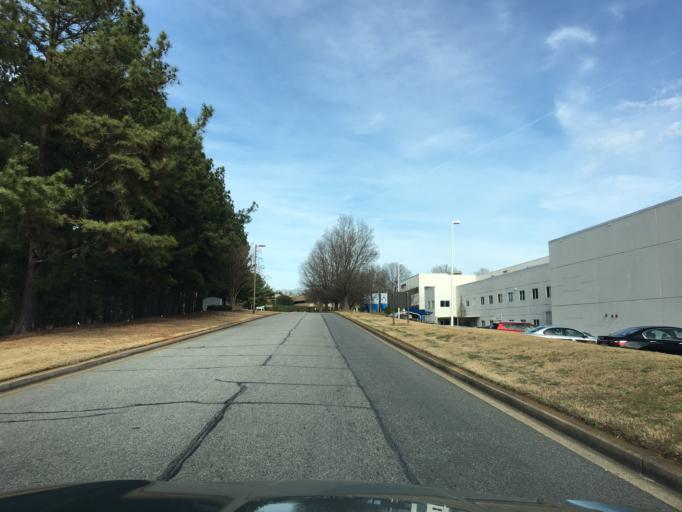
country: US
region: South Carolina
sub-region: Spartanburg County
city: Wellford
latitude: 34.9014
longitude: -82.1054
